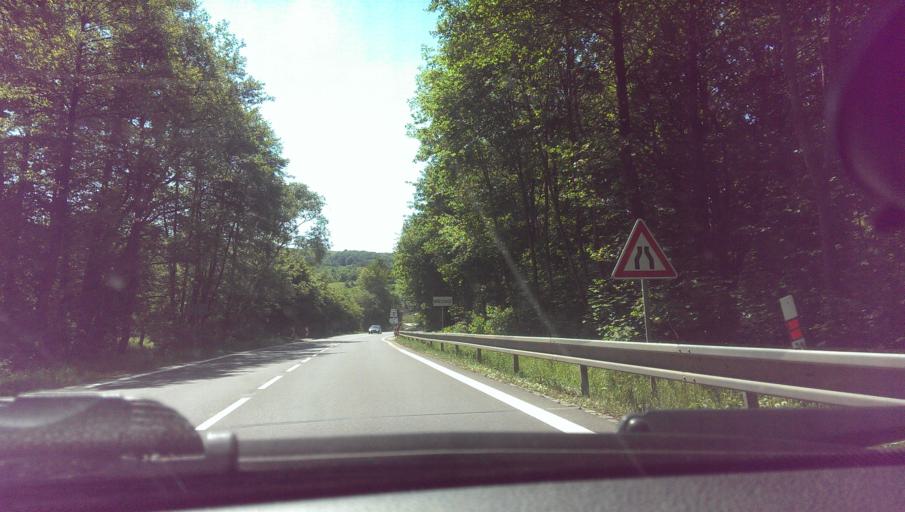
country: CZ
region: Zlin
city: Breznice
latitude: 49.1873
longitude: 17.6572
